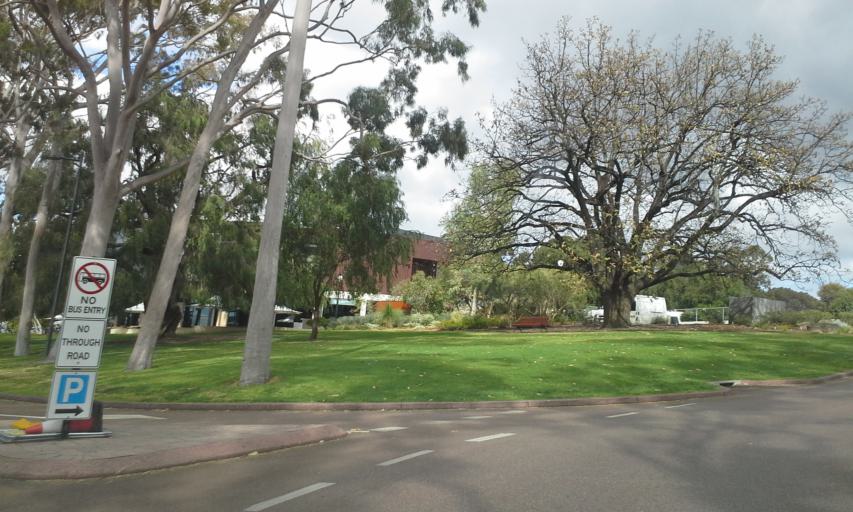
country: AU
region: Western Australia
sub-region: City of Perth
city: West Perth
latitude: -31.9588
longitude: 115.8440
